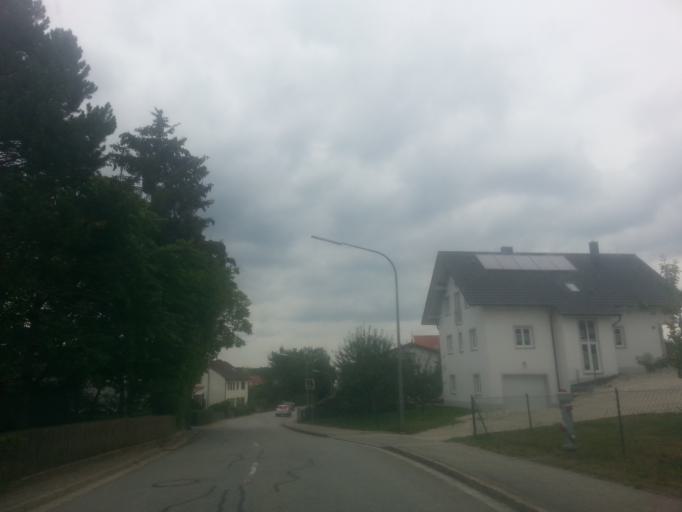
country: DE
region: Bavaria
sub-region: Lower Bavaria
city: Pfeffenhausen
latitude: 48.6738
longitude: 11.9232
